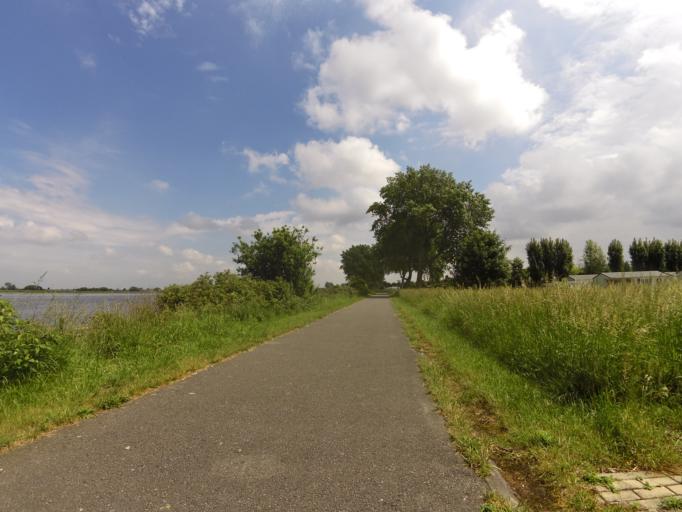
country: BE
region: Flanders
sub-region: Provincie West-Vlaanderen
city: Nieuwpoort
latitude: 51.1321
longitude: 2.7725
